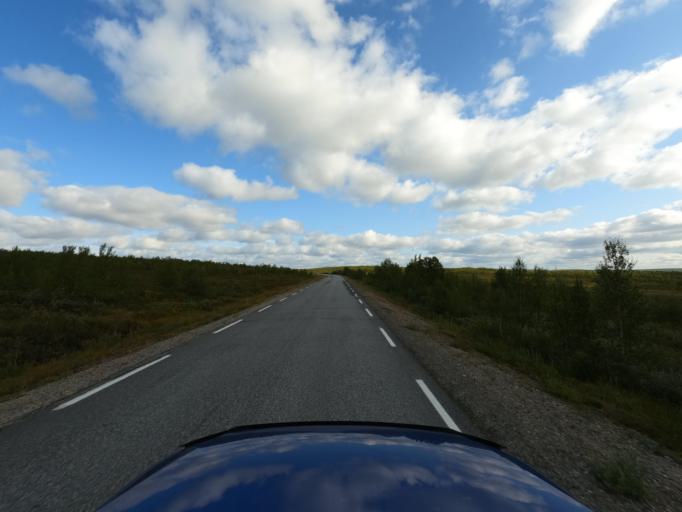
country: NO
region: Finnmark Fylke
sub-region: Porsanger
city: Lakselv
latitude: 69.3755
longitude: 24.4281
